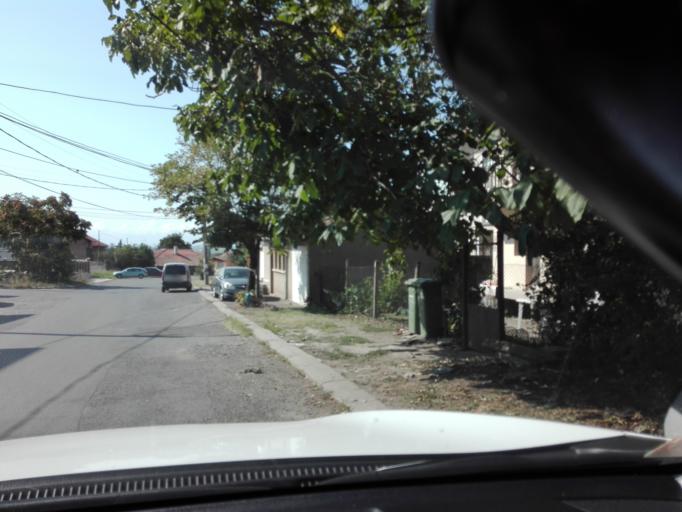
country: BG
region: Burgas
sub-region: Obshtina Kameno
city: Kameno
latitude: 42.6288
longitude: 27.3950
